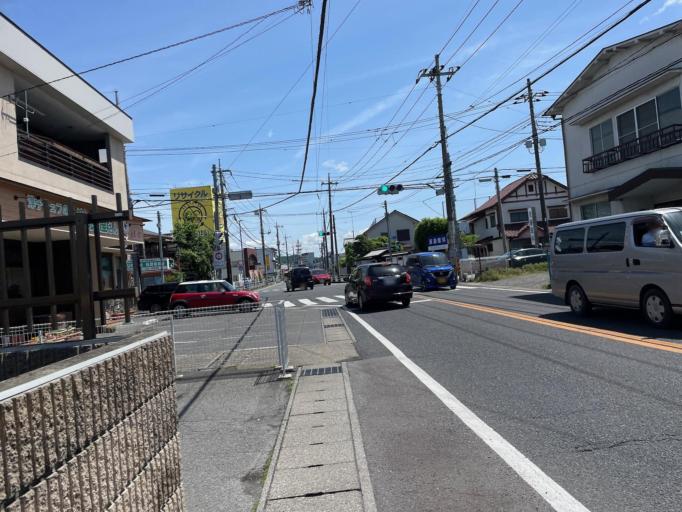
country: JP
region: Tochigi
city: Sano
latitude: 36.3133
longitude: 139.5840
